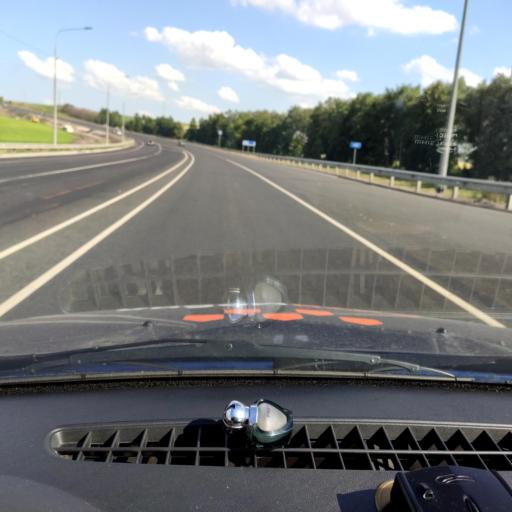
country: RU
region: Lipetsk
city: Yelets
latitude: 52.5806
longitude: 38.5130
